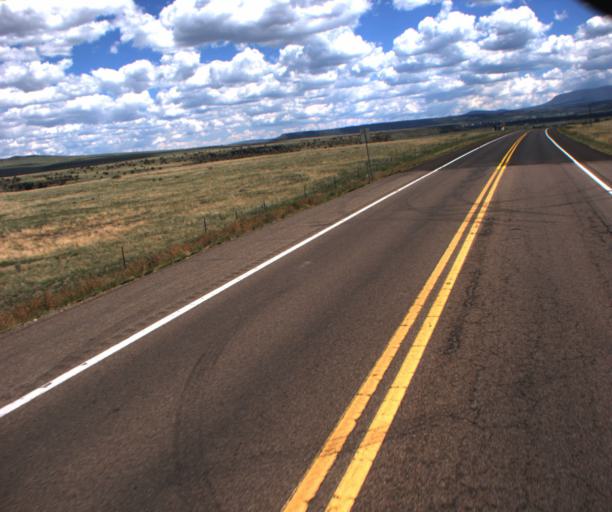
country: US
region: Arizona
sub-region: Apache County
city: Springerville
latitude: 34.1689
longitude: -109.3120
